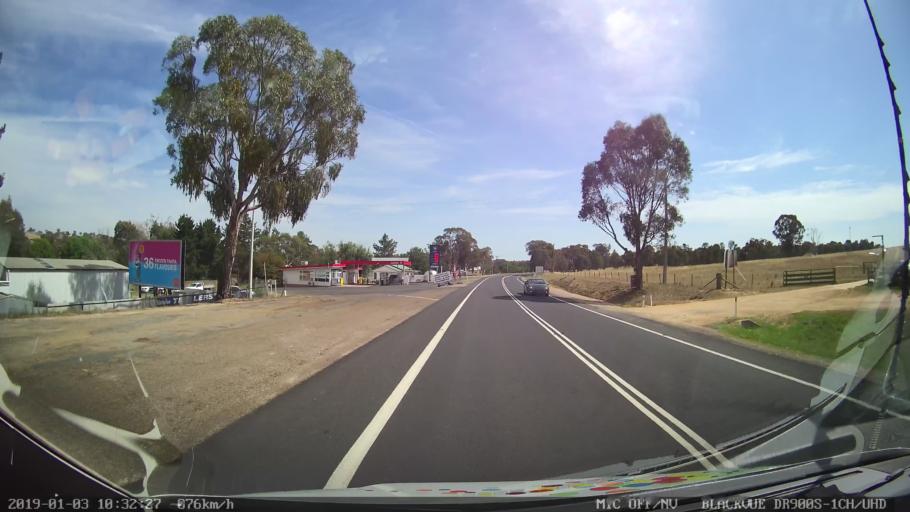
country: AU
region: New South Wales
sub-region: Young
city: Young
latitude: -34.3385
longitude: 148.2829
